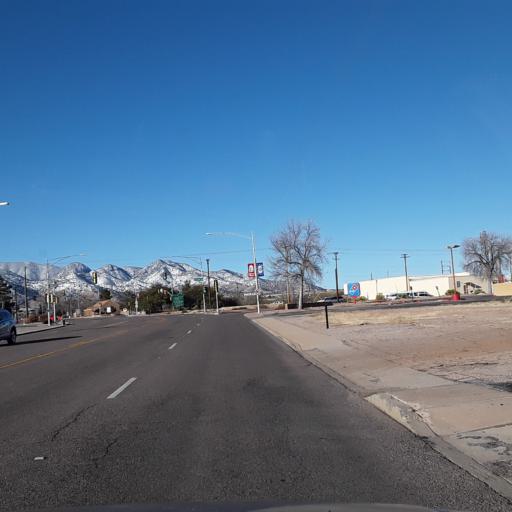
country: US
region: Arizona
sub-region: Cochise County
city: Sierra Vista
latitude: 31.5544
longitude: -110.3045
